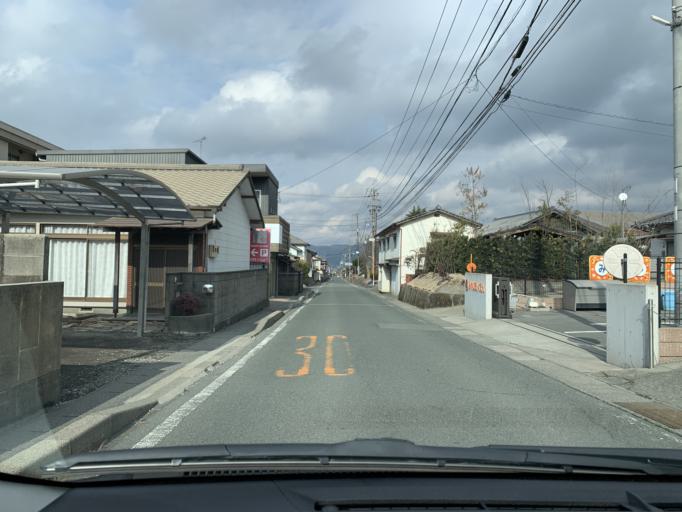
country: JP
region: Kumamoto
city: Aso
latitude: 32.9384
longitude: 131.1148
